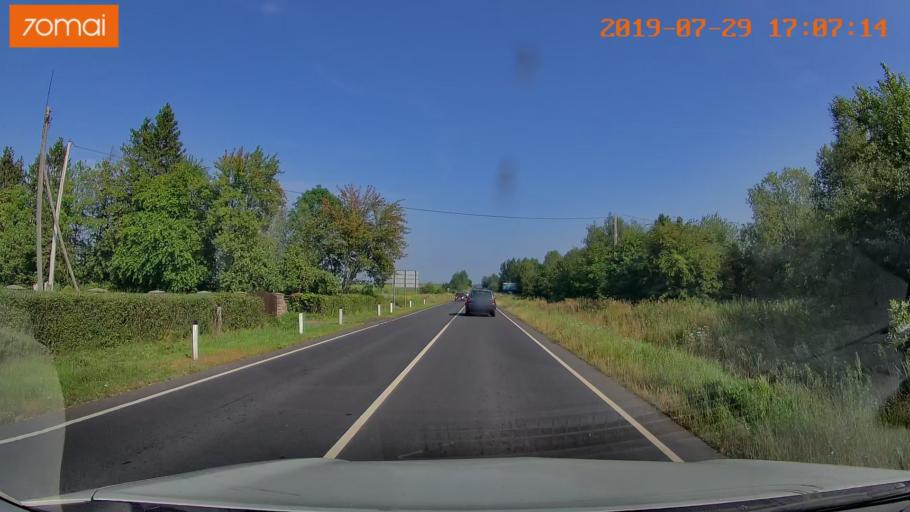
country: RU
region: Kaliningrad
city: Vzmorye
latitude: 54.8179
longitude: 20.3191
